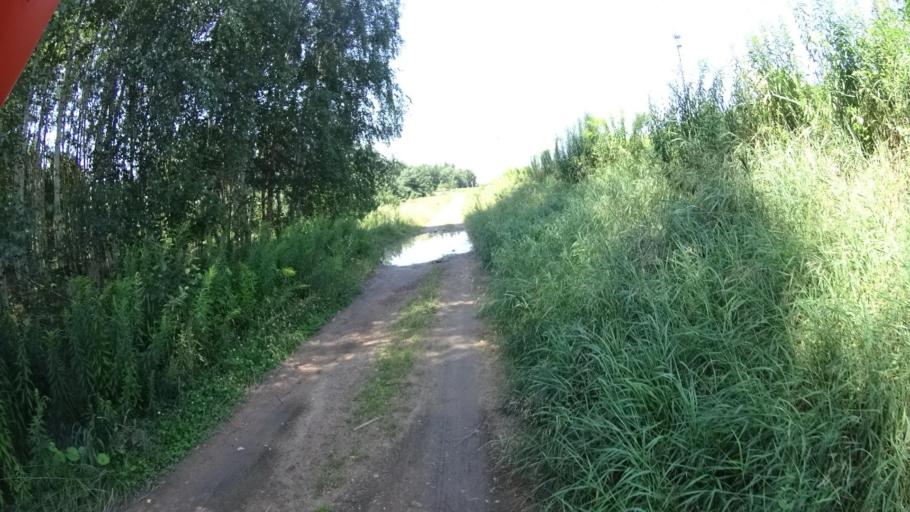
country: PL
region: Masovian Voivodeship
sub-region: Powiat piaseczynski
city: Tarczyn
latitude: 51.9706
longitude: 20.8571
